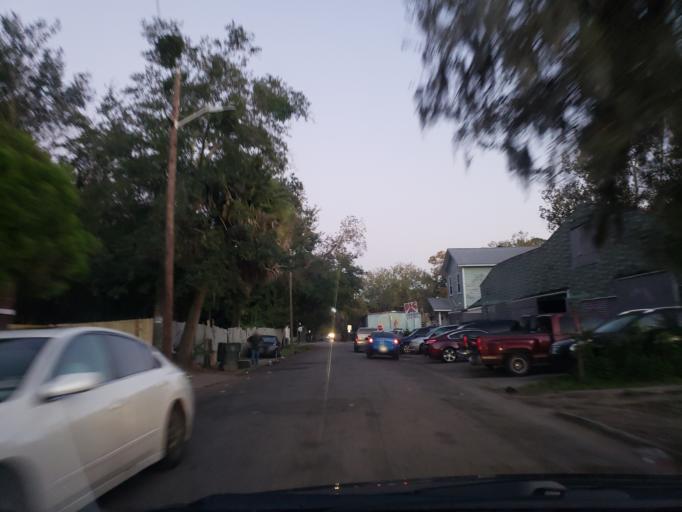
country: US
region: Georgia
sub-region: Chatham County
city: Savannah
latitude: 32.0518
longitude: -81.0849
